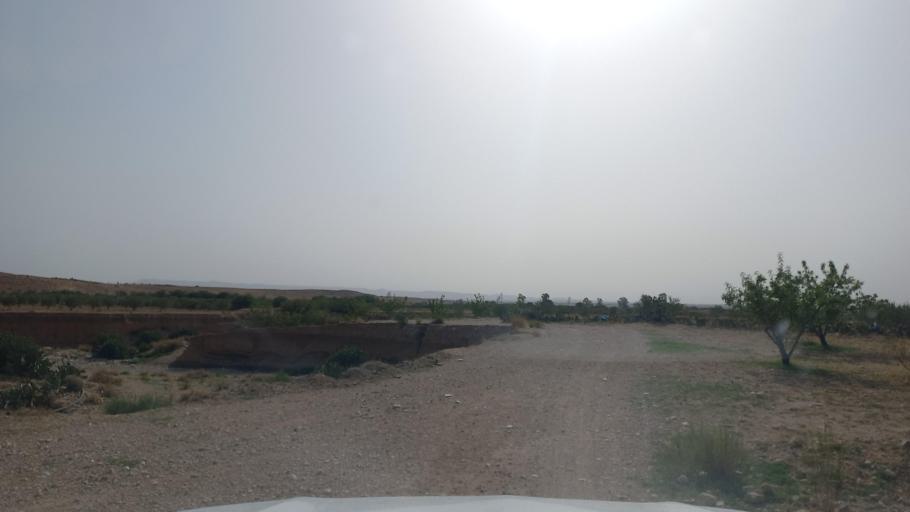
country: TN
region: Al Qasrayn
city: Kasserine
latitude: 35.2964
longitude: 8.9650
